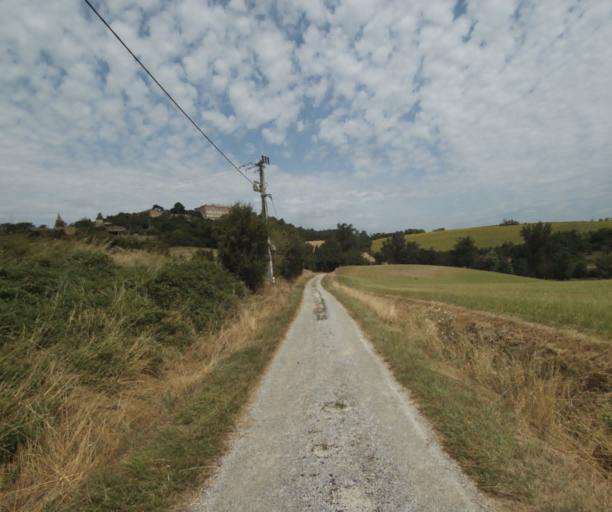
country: FR
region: Midi-Pyrenees
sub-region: Departement de la Haute-Garonne
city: Saint-Felix-Lauragais
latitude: 43.4445
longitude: 1.8917
